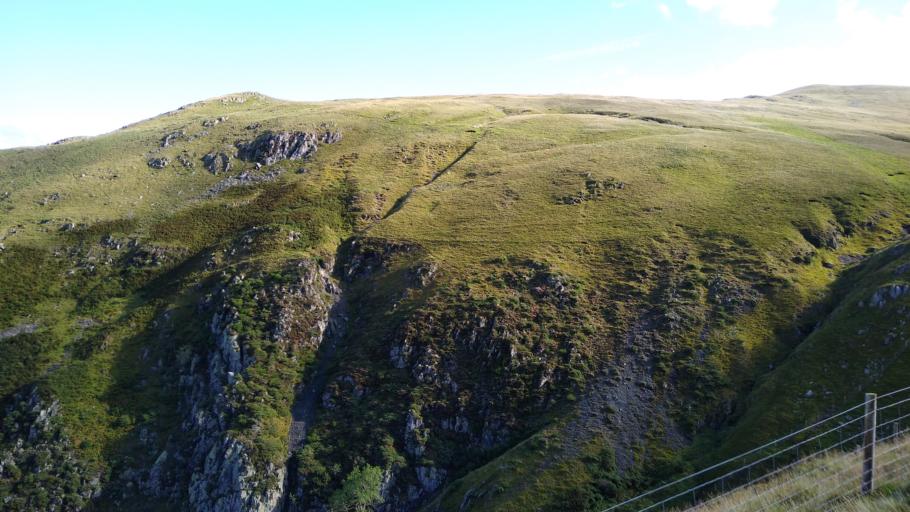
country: GB
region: England
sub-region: Cumbria
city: Keswick
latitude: 54.5597
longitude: -3.0430
